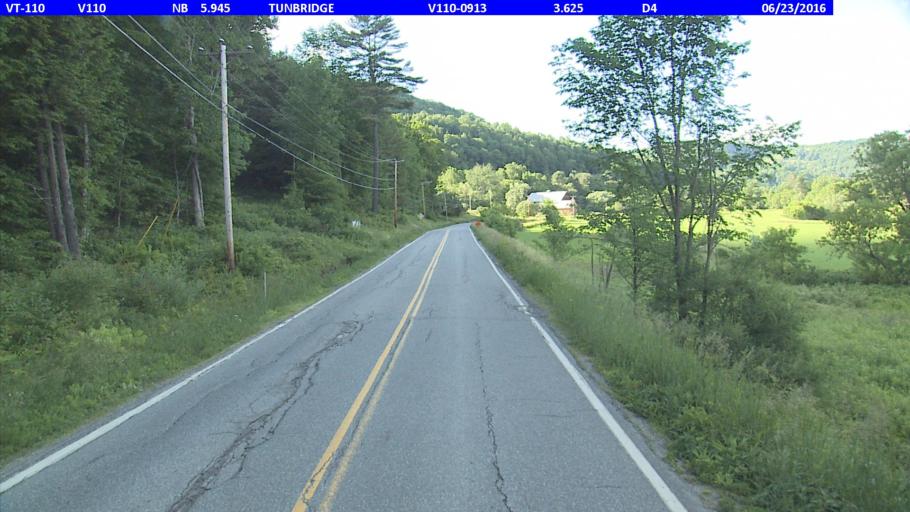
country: US
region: Vermont
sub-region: Orange County
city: Chelsea
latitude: 43.8975
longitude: -72.4857
